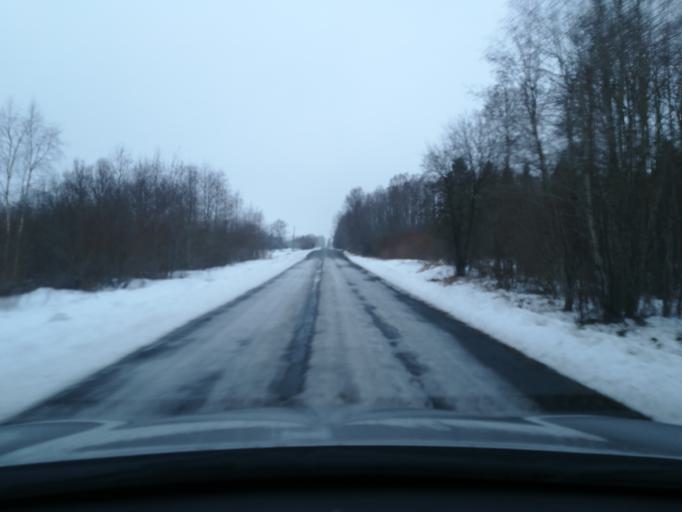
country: EE
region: Harju
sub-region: Raasiku vald
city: Raasiku
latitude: 59.3420
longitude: 25.2262
